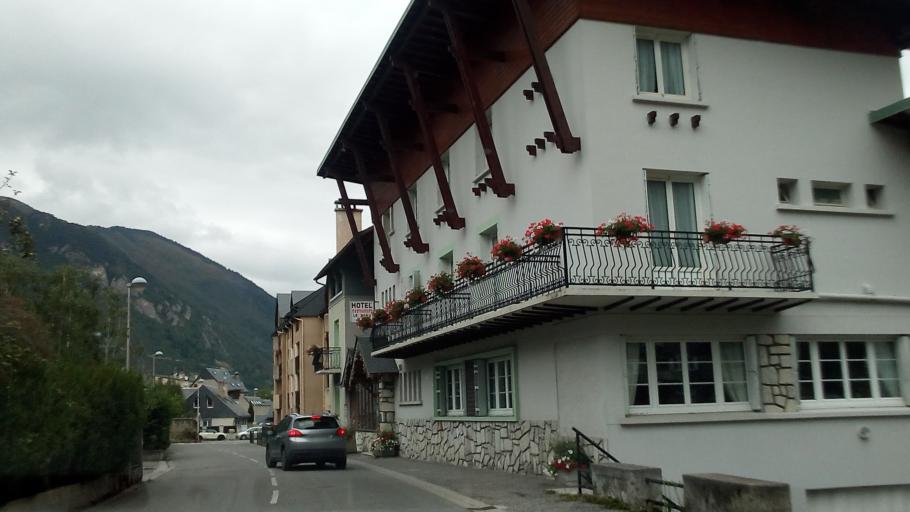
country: FR
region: Midi-Pyrenees
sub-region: Departement des Hautes-Pyrenees
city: Saint-Lary-Soulan
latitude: 42.8143
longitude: 0.3211
